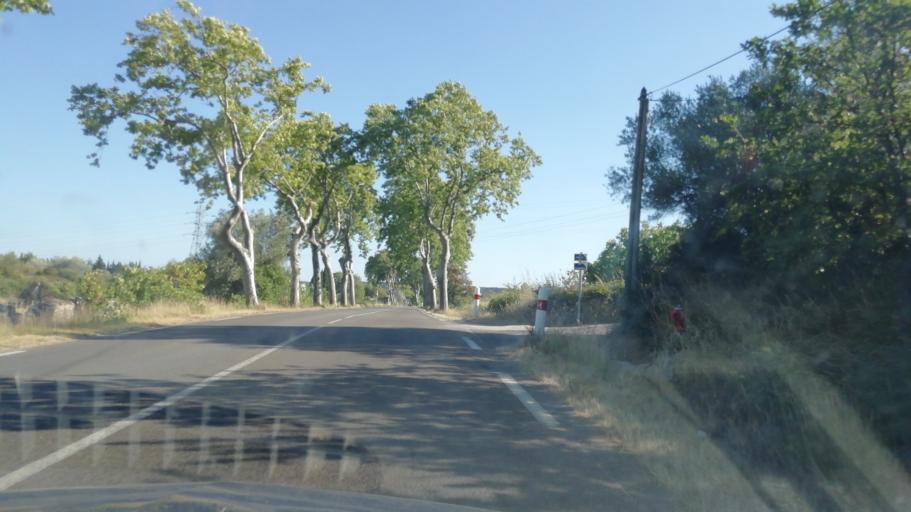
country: FR
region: Languedoc-Roussillon
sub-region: Departement de l'Herault
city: Nebian
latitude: 43.6140
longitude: 3.4368
